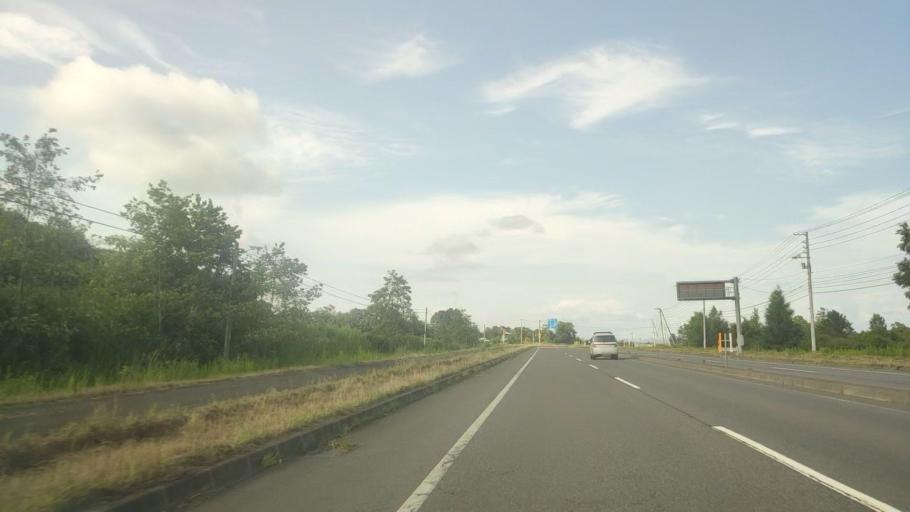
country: JP
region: Hokkaido
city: Chitose
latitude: 42.7736
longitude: 141.8265
